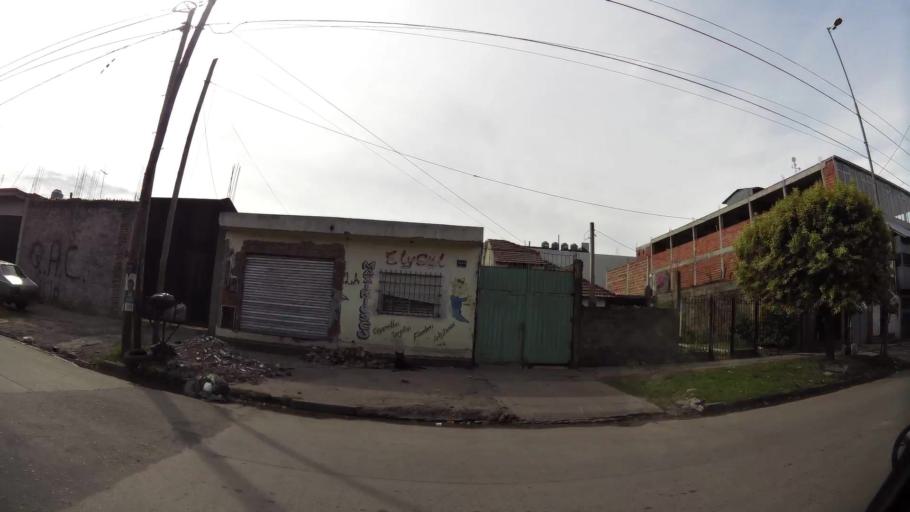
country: AR
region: Buenos Aires
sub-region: Partido de Quilmes
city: Quilmes
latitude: -34.7669
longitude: -58.2543
